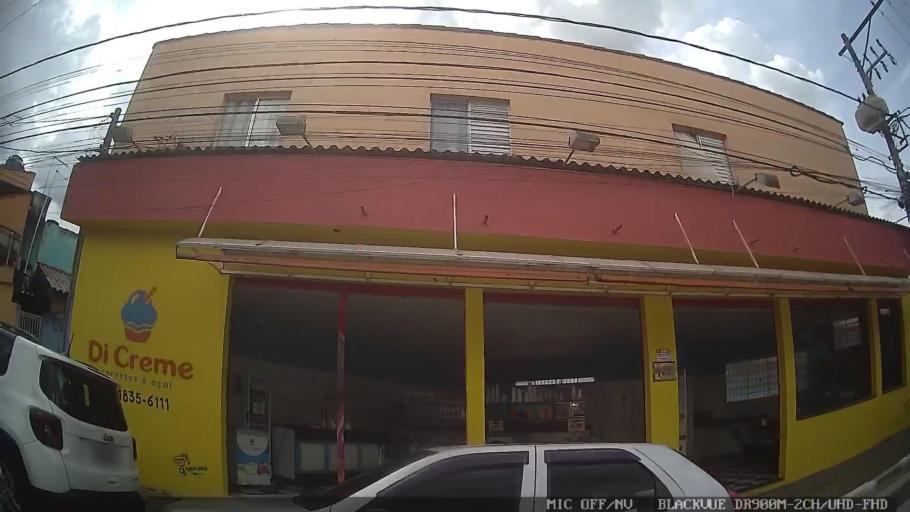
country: BR
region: Sao Paulo
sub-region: Poa
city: Poa
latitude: -23.5287
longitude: -46.3374
